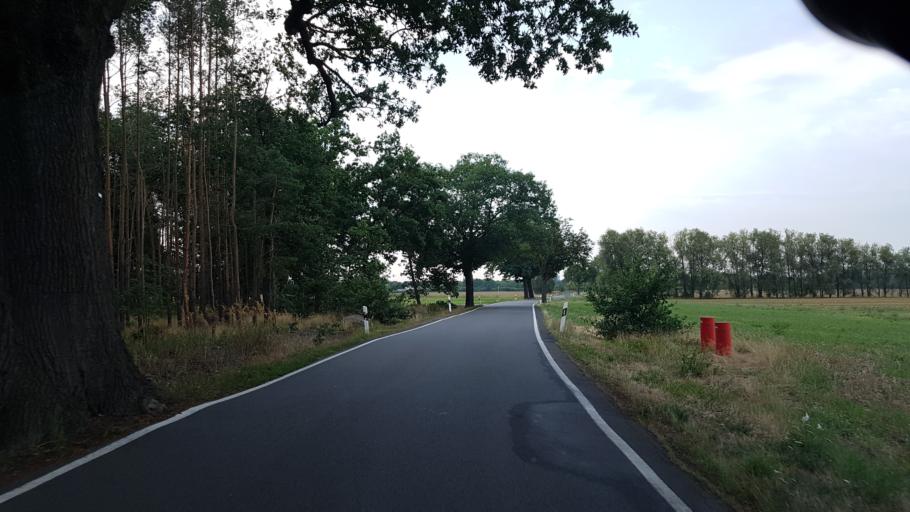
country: DE
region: Brandenburg
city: Lindenau
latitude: 51.3904
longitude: 13.7453
